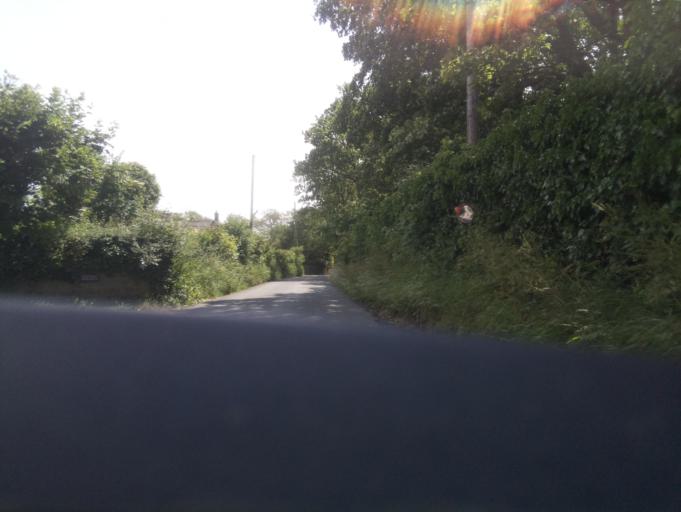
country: GB
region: Wales
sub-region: Vale of Glamorgan
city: Wick
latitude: 51.4044
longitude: -3.5289
